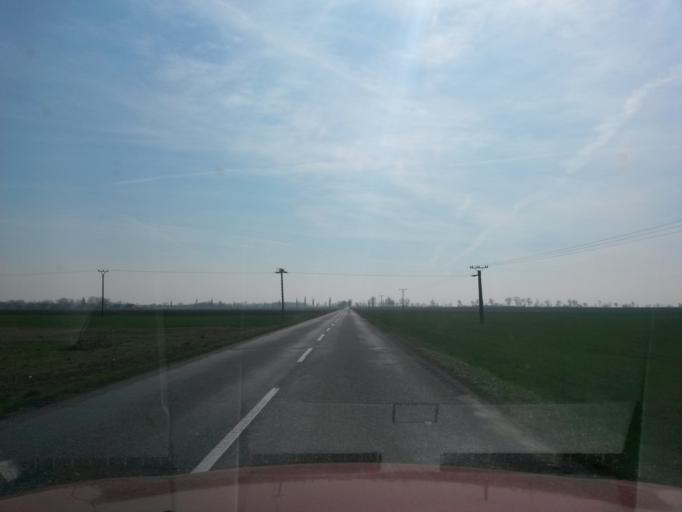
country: SK
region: Nitriansky
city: Levice
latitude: 48.1562
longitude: 18.5632
